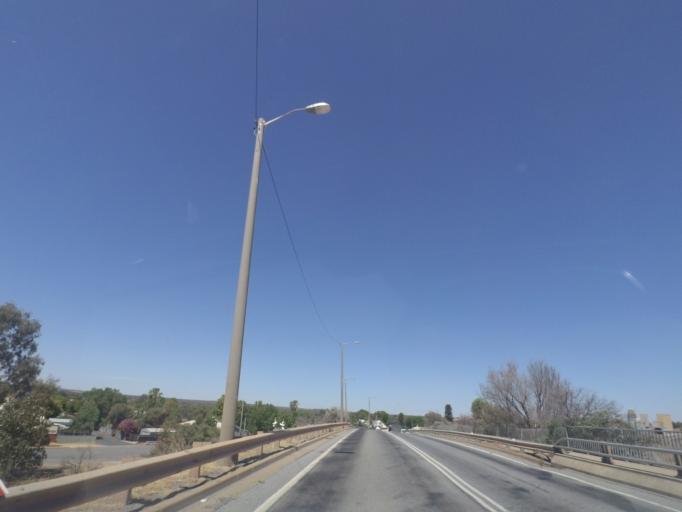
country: AU
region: New South Wales
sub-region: Narrandera
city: Narrandera
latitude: -34.7405
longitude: 146.5594
